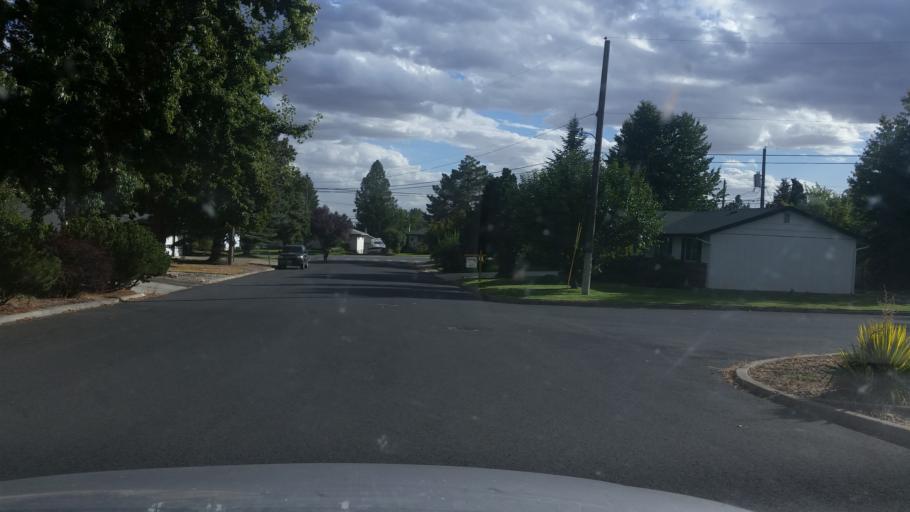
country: US
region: Washington
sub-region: Spokane County
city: Cheney
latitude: 47.4826
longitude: -117.5922
